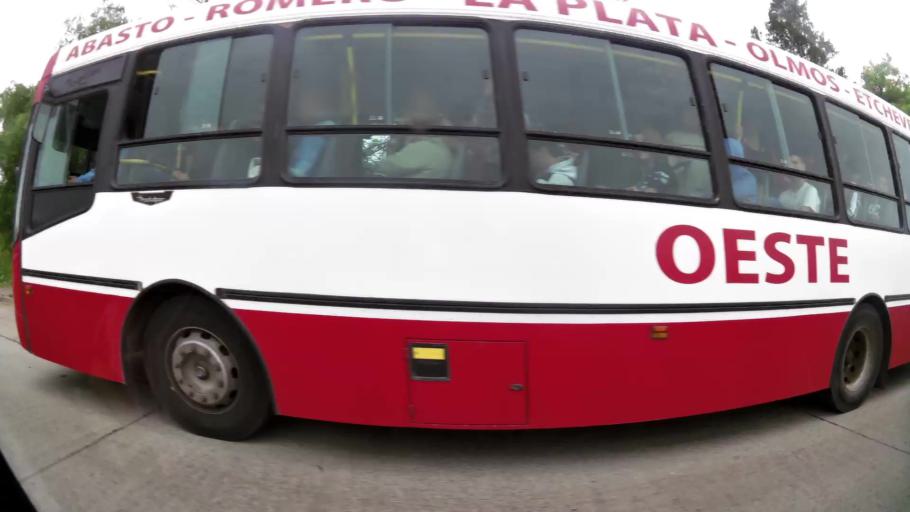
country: AR
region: Buenos Aires
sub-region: Partido de La Plata
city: La Plata
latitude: -34.9679
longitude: -58.0179
